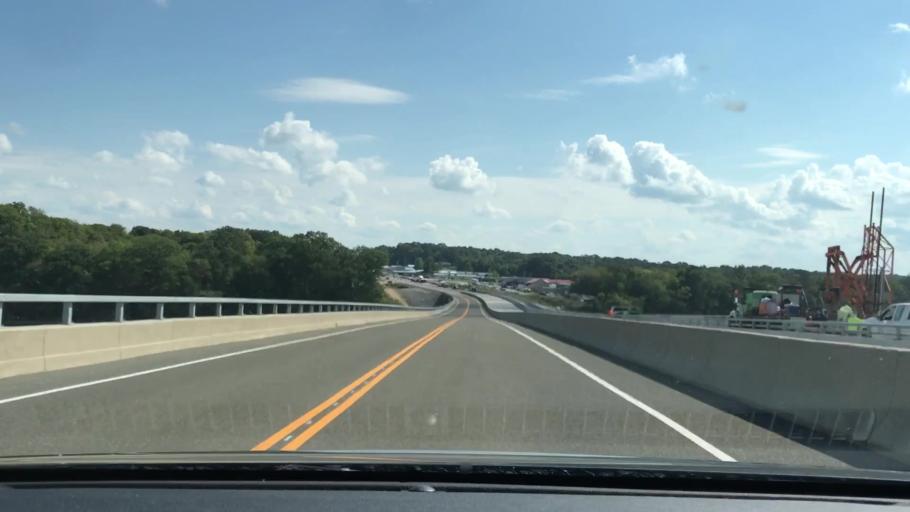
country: US
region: Kentucky
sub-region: Trigg County
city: Cadiz
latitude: 36.7995
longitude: -87.9741
